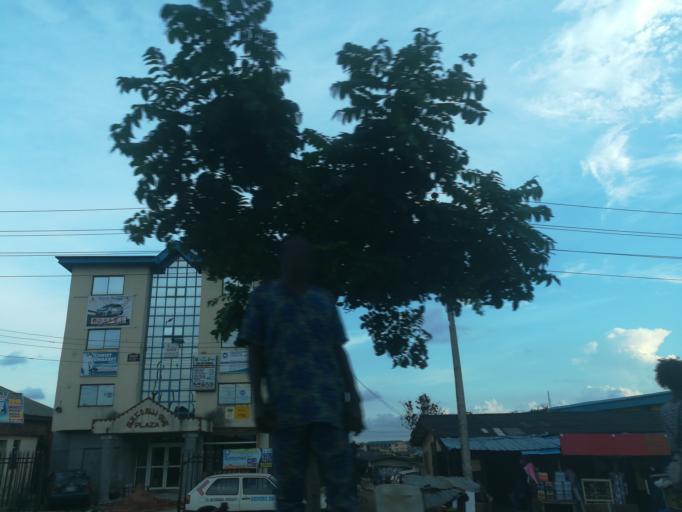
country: NG
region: Lagos
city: Ebute Ikorodu
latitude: 6.6193
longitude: 3.4759
